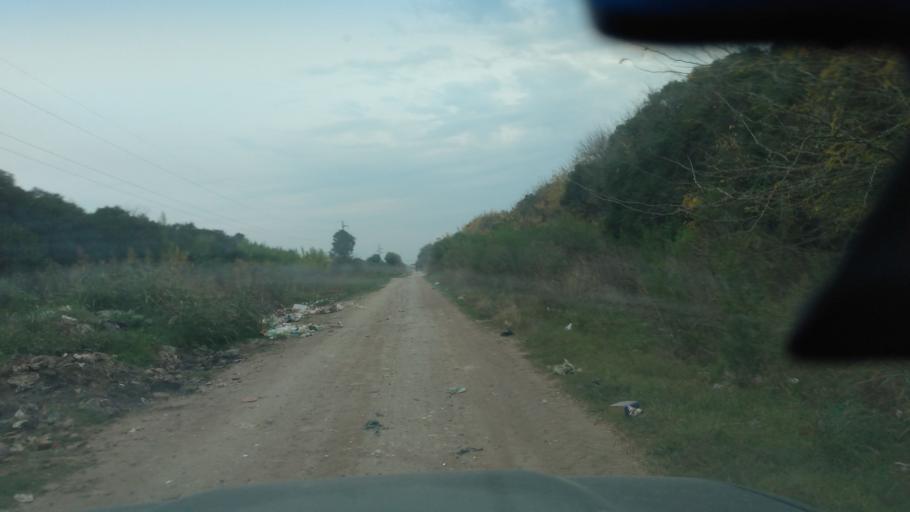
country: AR
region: Buenos Aires
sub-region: Partido de Lujan
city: Lujan
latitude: -34.5572
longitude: -59.1472
